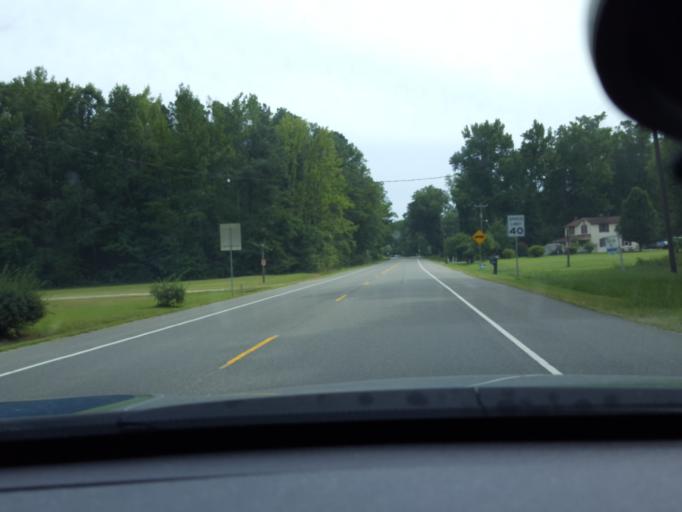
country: US
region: Virginia
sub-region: Hanover County
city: Hanover
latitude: 37.7732
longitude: -77.3711
